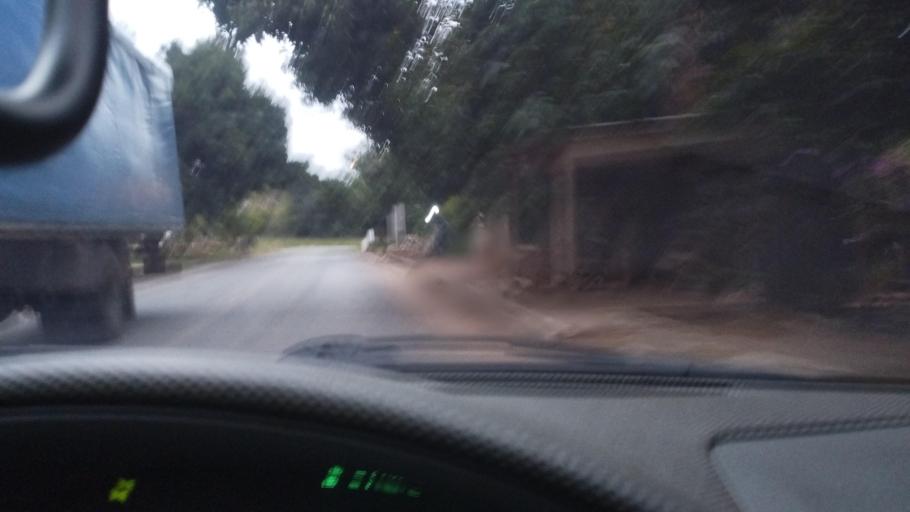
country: PY
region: Central
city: Fernando de la Mora
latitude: -25.2894
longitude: -57.5146
